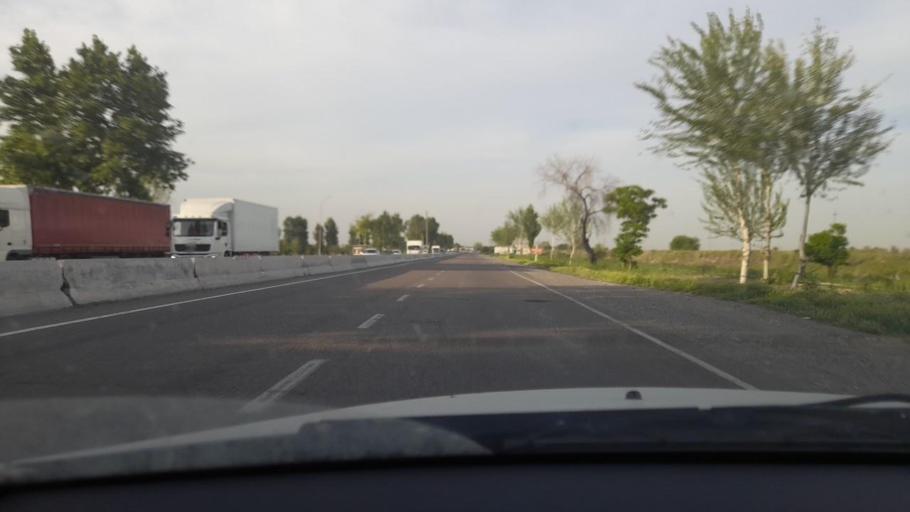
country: KZ
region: Ongtustik Qazaqstan
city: Myrzakent
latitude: 40.5532
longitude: 68.3634
